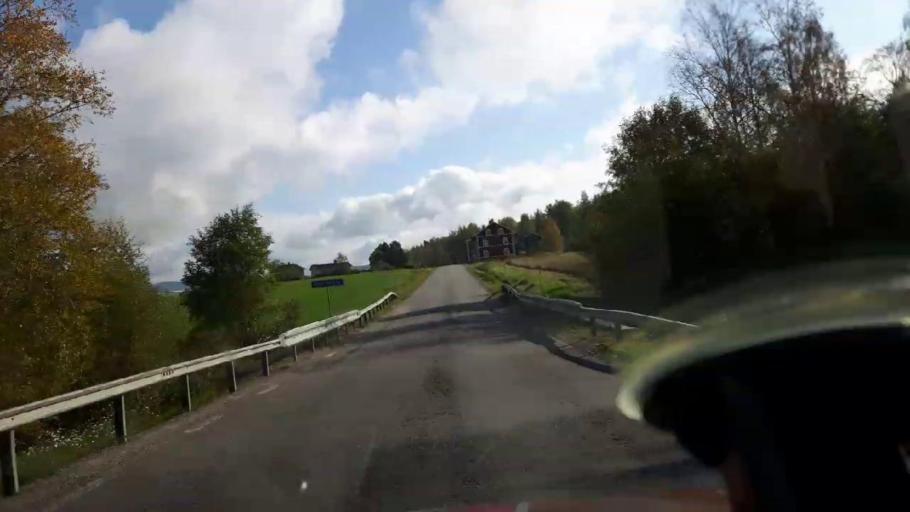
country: SE
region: Gaevleborg
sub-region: Ljusdals Kommun
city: Jaervsoe
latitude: 61.7534
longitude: 16.1341
